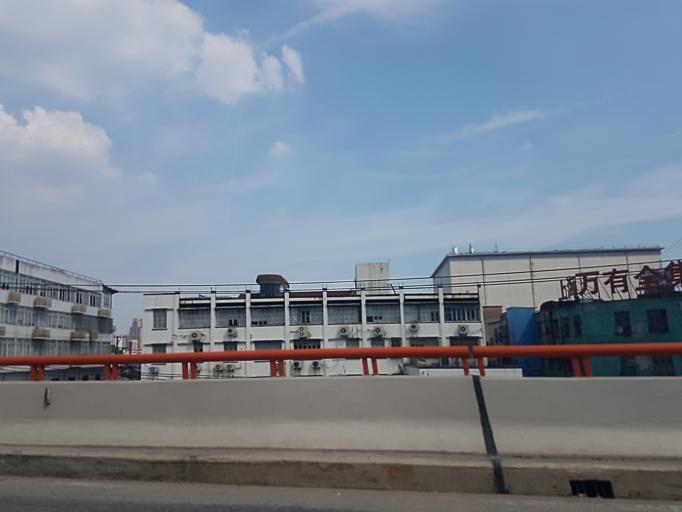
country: CN
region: Shanghai Shi
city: Luwan
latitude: 31.2122
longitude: 121.4985
